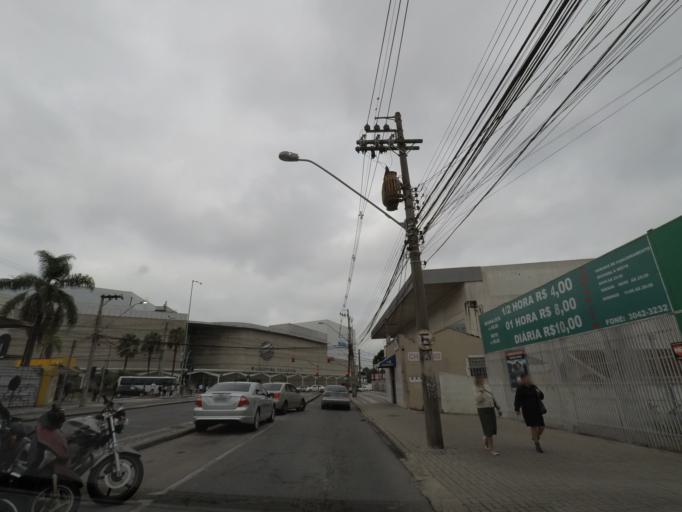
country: BR
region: Parana
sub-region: Curitiba
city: Curitiba
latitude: -25.4771
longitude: -49.2925
